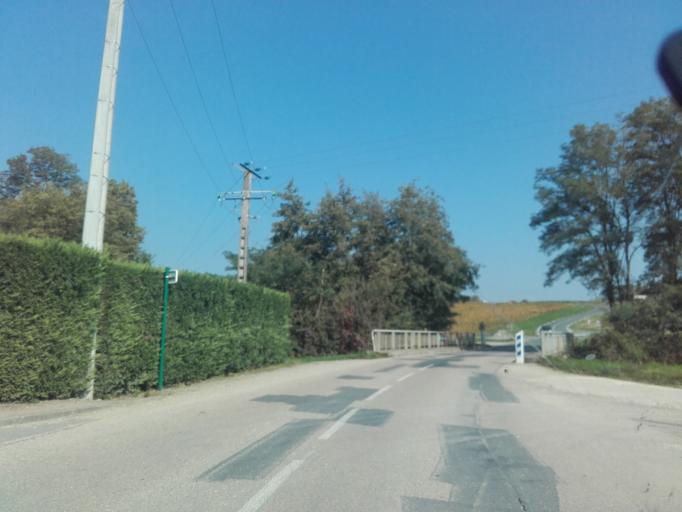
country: FR
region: Bourgogne
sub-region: Departement de Saone-et-Loire
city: La Chapelle-de-Guinchay
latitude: 46.2203
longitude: 4.7441
